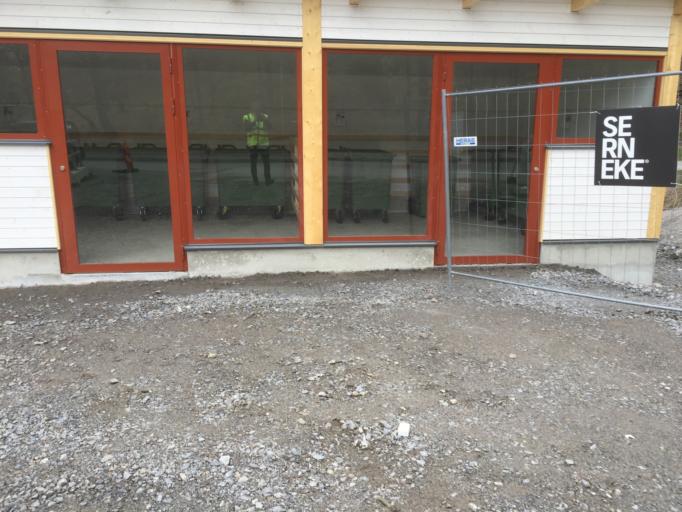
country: SE
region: Stockholm
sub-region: Huddinge Kommun
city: Segeltorp
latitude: 59.2891
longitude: 17.9076
